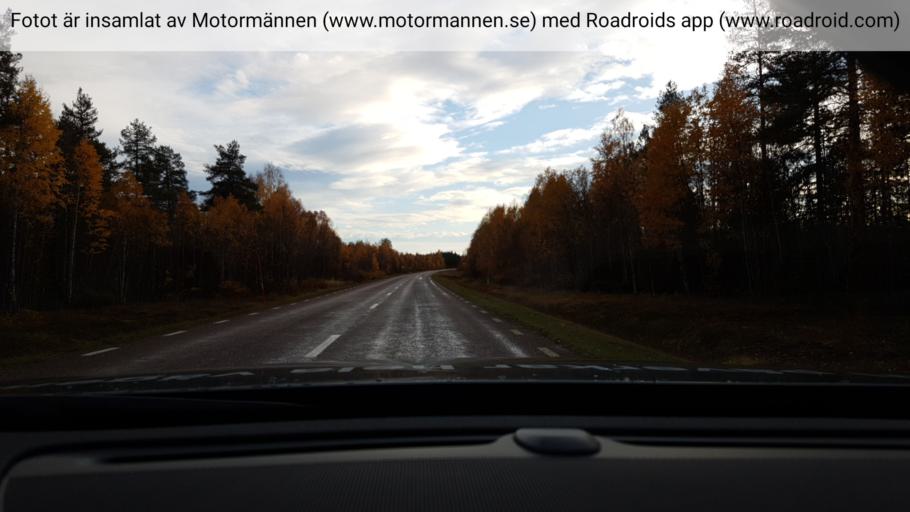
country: SE
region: Norrbotten
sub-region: Pajala Kommun
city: Pajala
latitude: 67.1533
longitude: 22.6290
